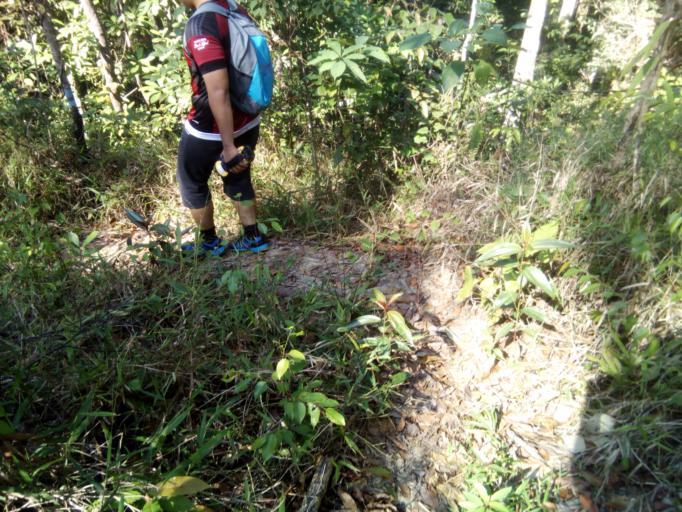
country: MY
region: Penang
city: Tanjung Tokong
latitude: 5.4284
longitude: 100.2829
